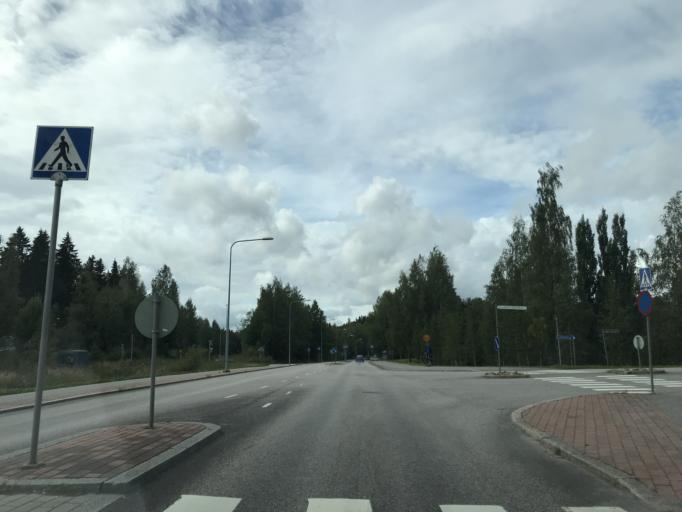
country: FI
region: Paijanne Tavastia
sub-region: Lahti
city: Lahti
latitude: 60.9910
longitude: 25.7431
